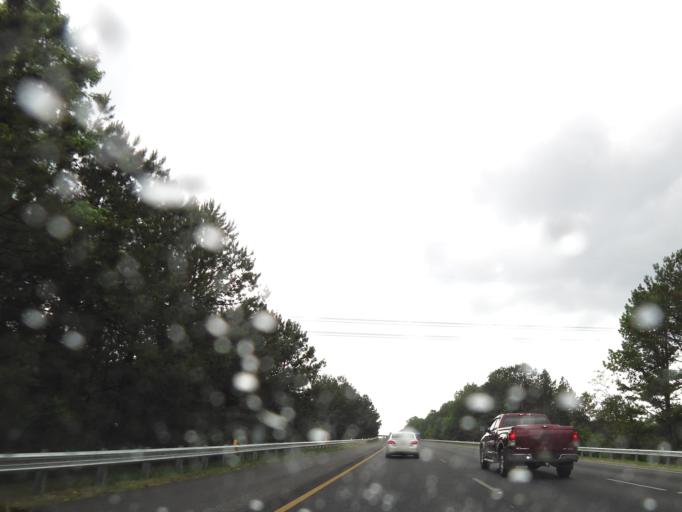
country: US
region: Georgia
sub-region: Carroll County
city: Villa Rica
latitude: 33.7230
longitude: -84.8704
